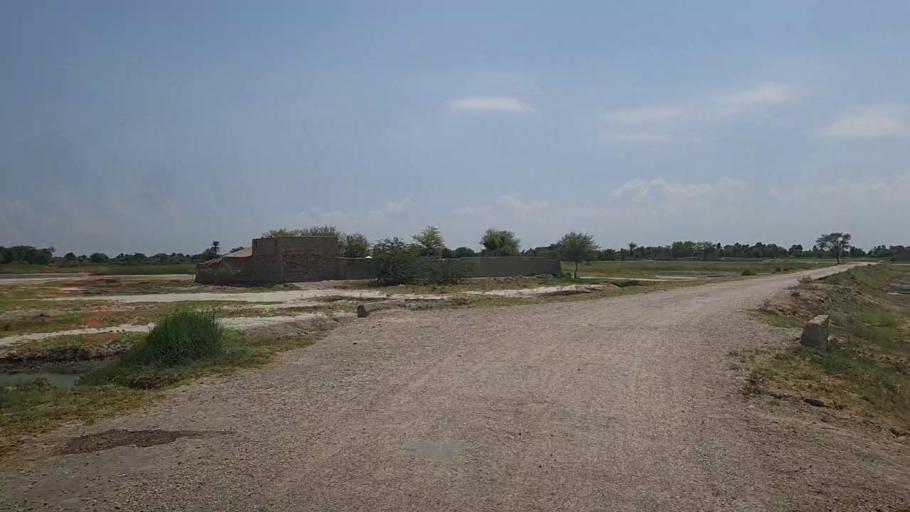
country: PK
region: Sindh
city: Ubauro
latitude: 28.1547
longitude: 69.7649
